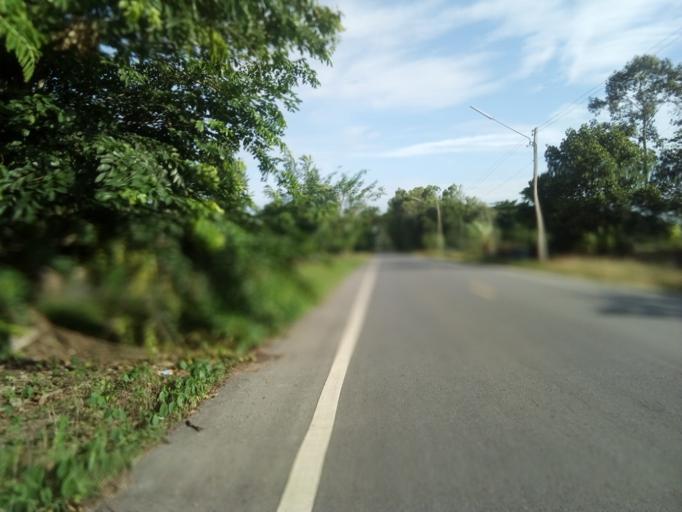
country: TH
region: Pathum Thani
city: Nong Suea
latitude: 14.1175
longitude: 100.8460
